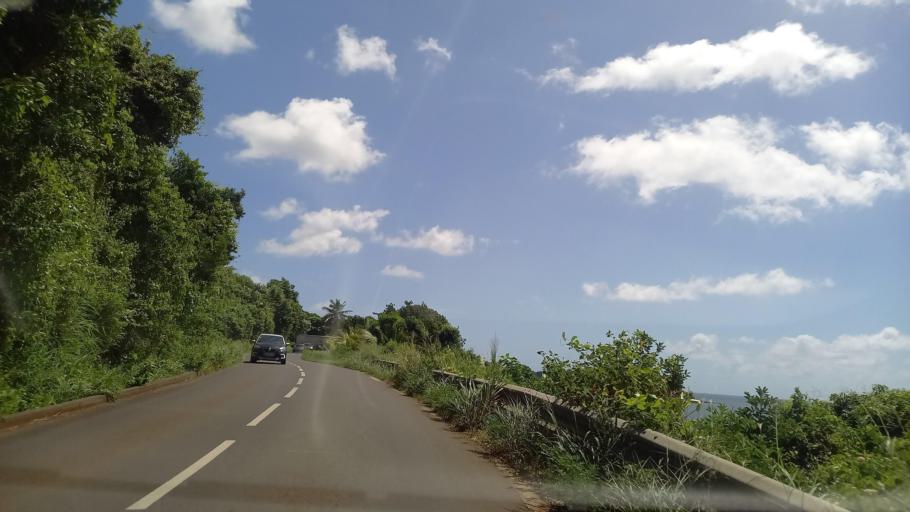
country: YT
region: Bandraboua
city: Bandraboua
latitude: -12.7177
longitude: 45.1300
